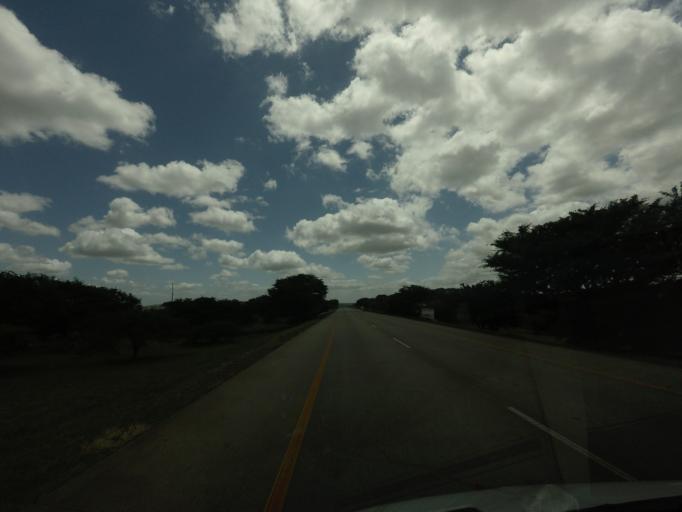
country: ZA
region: KwaZulu-Natal
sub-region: uMkhanyakude District Municipality
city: Mtubatuba
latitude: -28.4724
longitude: 32.1456
